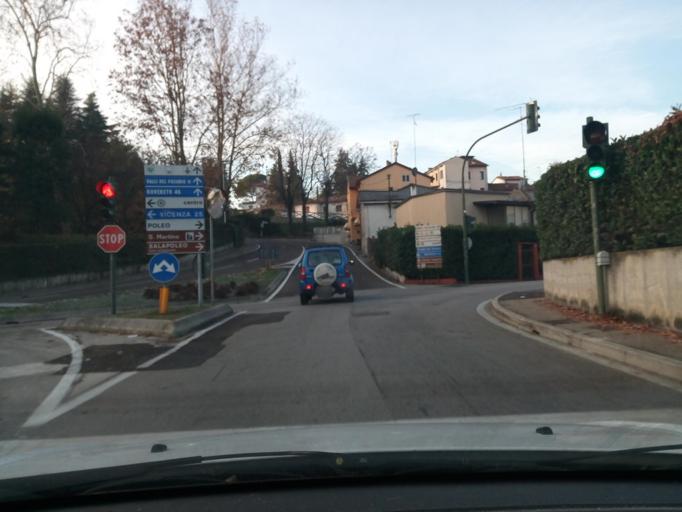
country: IT
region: Veneto
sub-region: Provincia di Vicenza
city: Schio
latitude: 45.7196
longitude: 11.3536
